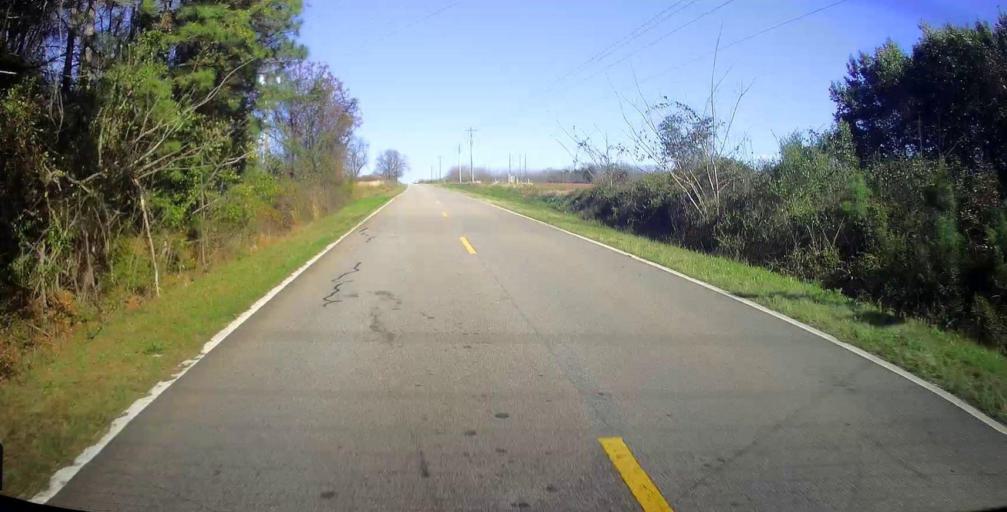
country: US
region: Georgia
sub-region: Peach County
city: Byron
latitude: 32.6444
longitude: -83.8185
